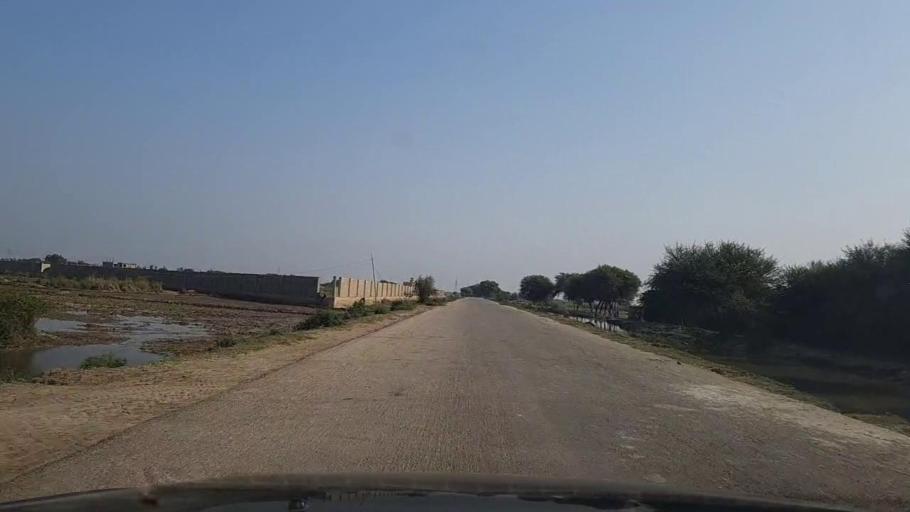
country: PK
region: Sindh
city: Chuhar Jamali
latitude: 24.5912
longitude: 68.0787
